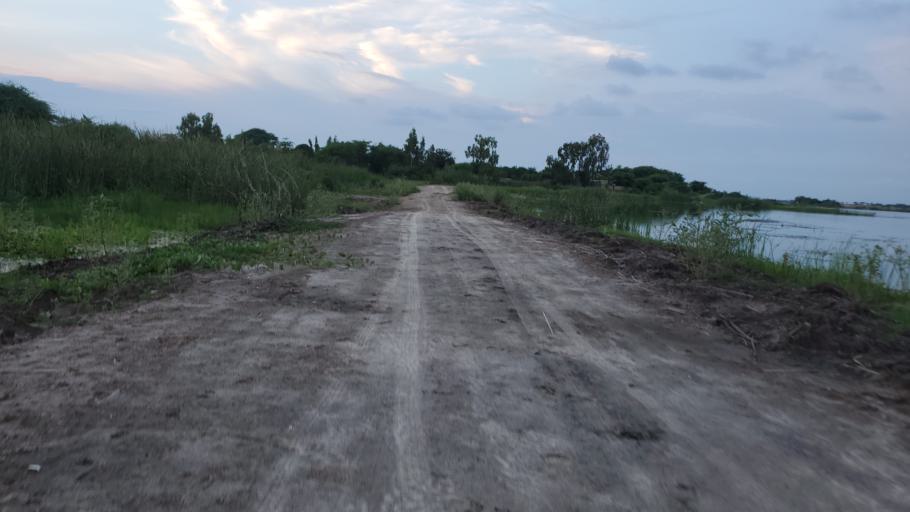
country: SN
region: Saint-Louis
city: Saint-Louis
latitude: 16.0370
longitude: -16.4172
